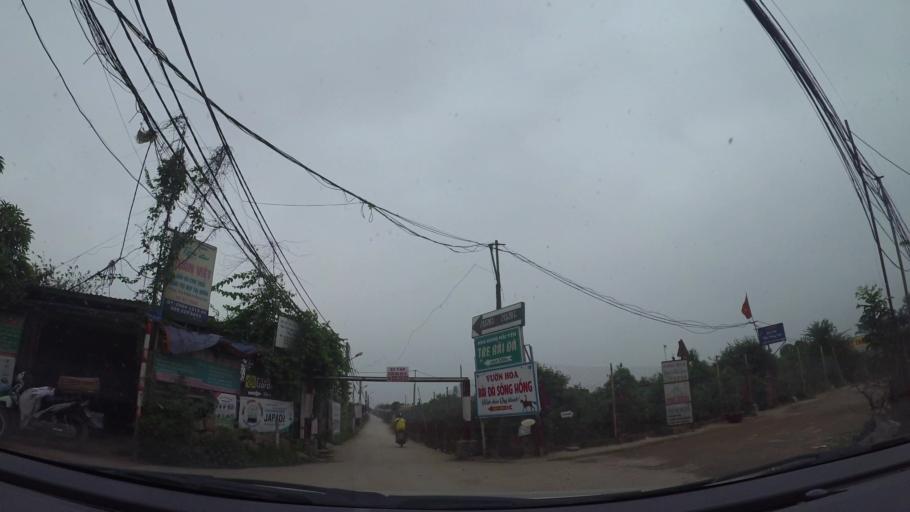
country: VN
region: Ha Noi
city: Tay Ho
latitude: 21.0738
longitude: 105.8285
